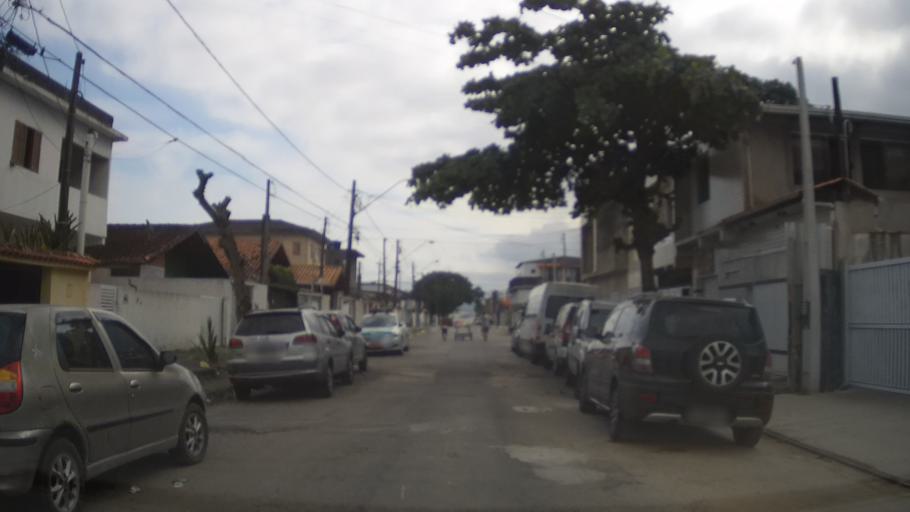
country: BR
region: Sao Paulo
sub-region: Praia Grande
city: Praia Grande
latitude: -24.0095
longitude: -46.4503
